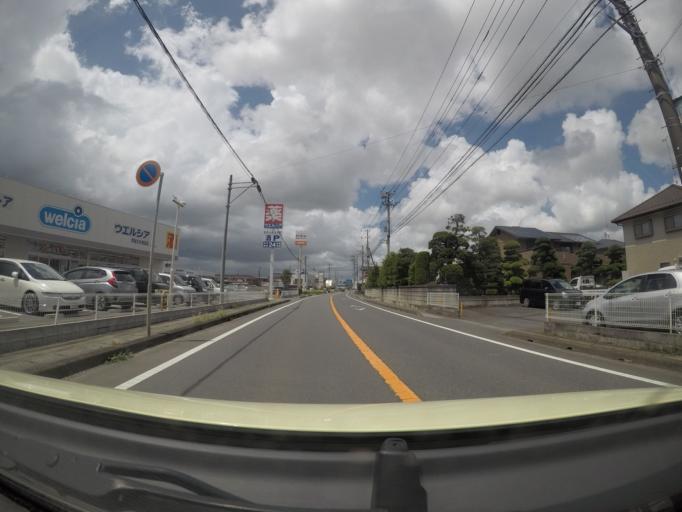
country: JP
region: Ibaraki
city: Mitsukaido
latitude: 36.0330
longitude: 139.9884
